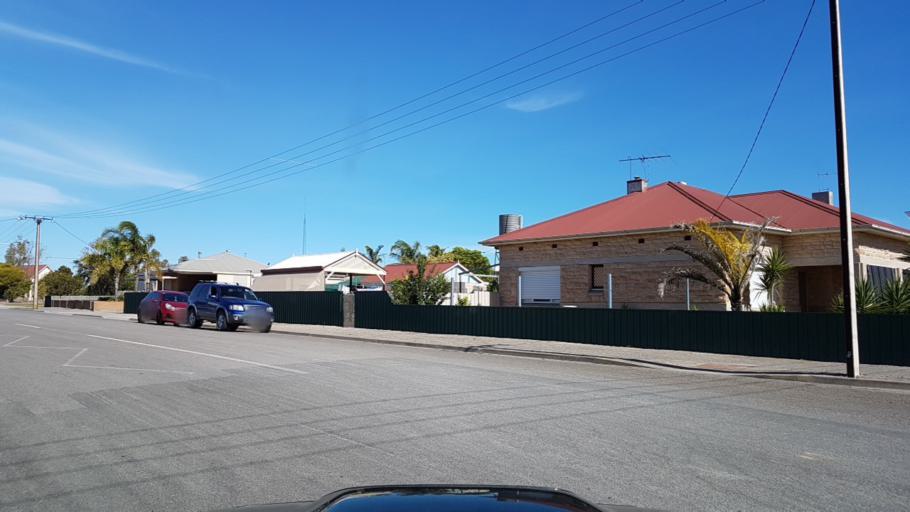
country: AU
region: South Australia
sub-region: Yorke Peninsula
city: Honiton
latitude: -34.9911
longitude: 137.3985
